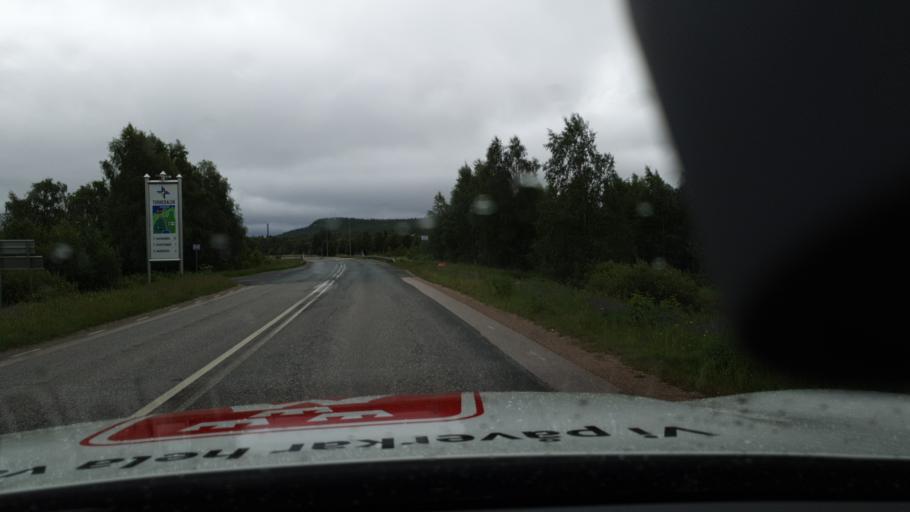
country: SE
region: Norrbotten
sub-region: Overtornea Kommun
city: OEvertornea
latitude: 66.3990
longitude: 23.6234
